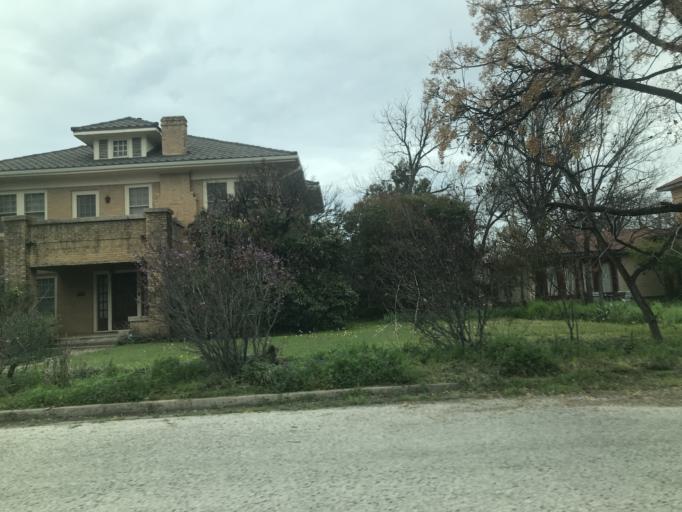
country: US
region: Texas
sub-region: Taylor County
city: Abilene
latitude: 32.4601
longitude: -99.7454
